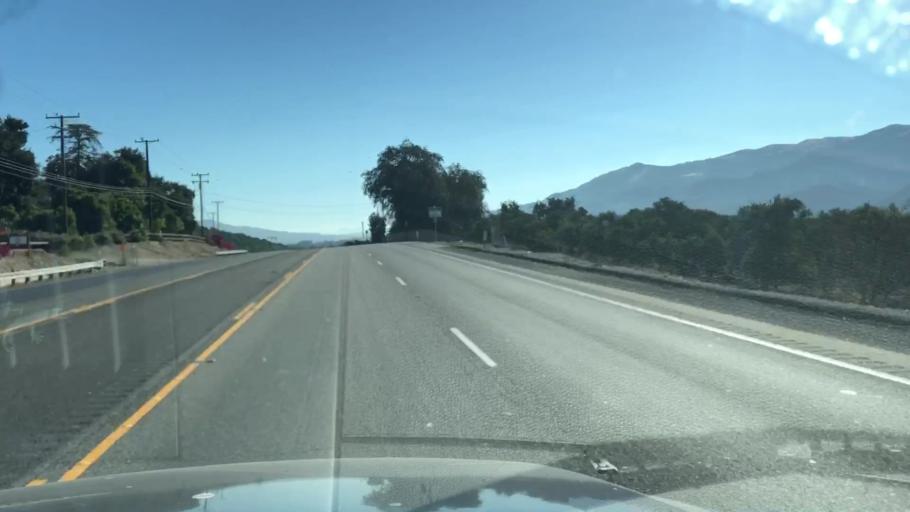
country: US
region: California
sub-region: Ventura County
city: Fillmore
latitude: 34.3962
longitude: -118.8627
